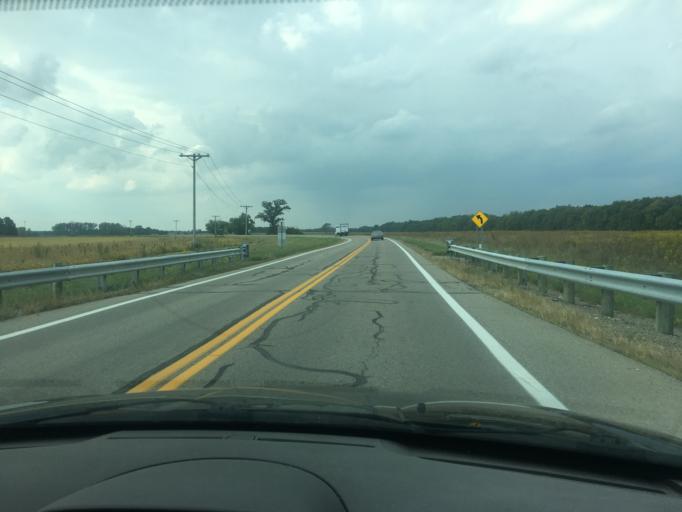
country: US
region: Ohio
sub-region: Champaign County
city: Urbana
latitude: 40.1554
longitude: -83.7886
